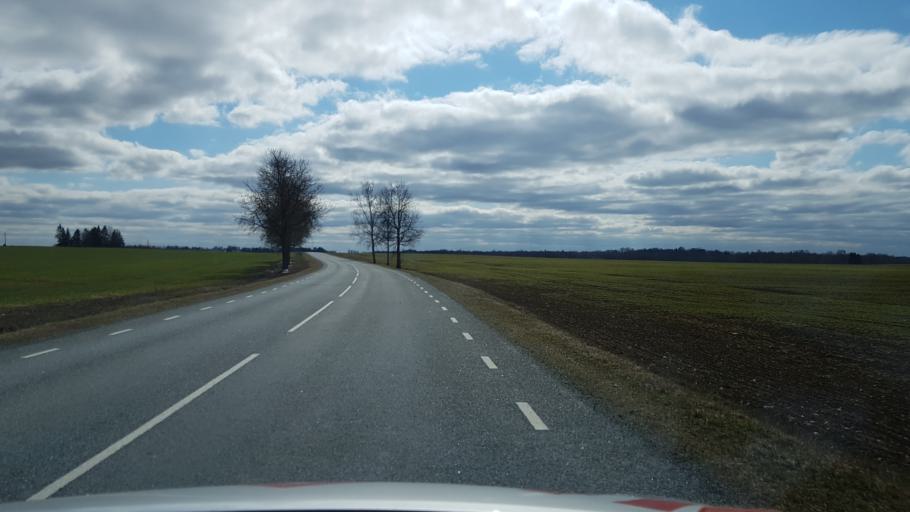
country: EE
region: Laeaene-Virumaa
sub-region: Kadrina vald
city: Kadrina
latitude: 59.3618
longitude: 26.1094
